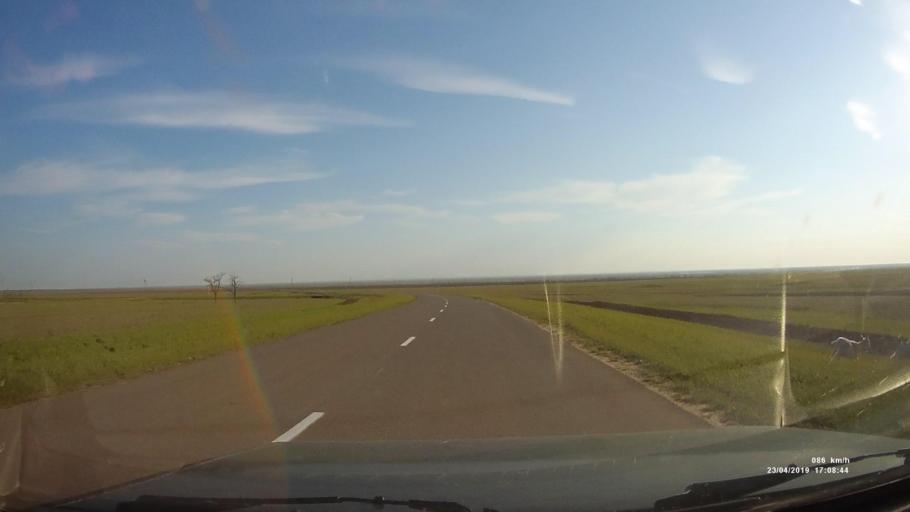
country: RU
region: Kalmykiya
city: Priyutnoye
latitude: 46.2676
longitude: 43.4853
